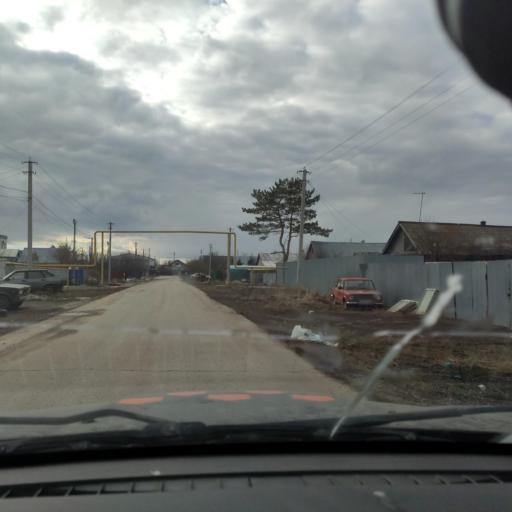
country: RU
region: Samara
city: Tol'yatti
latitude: 53.5739
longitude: 49.3071
